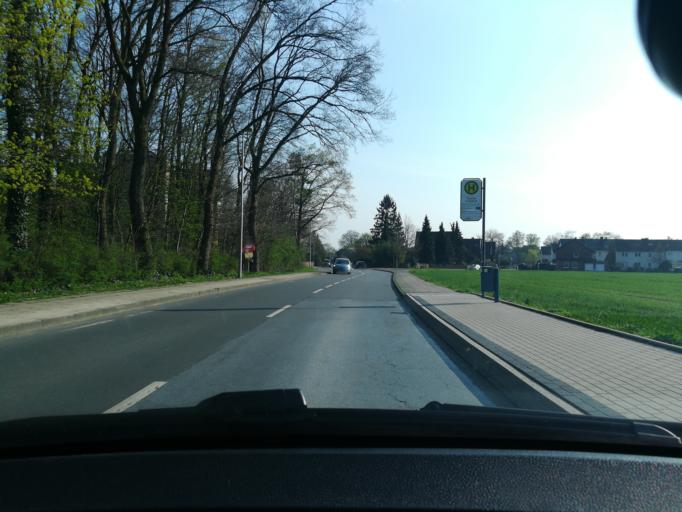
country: DE
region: North Rhine-Westphalia
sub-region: Regierungsbezirk Detmold
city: Bielefeld
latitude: 51.9994
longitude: 8.4745
